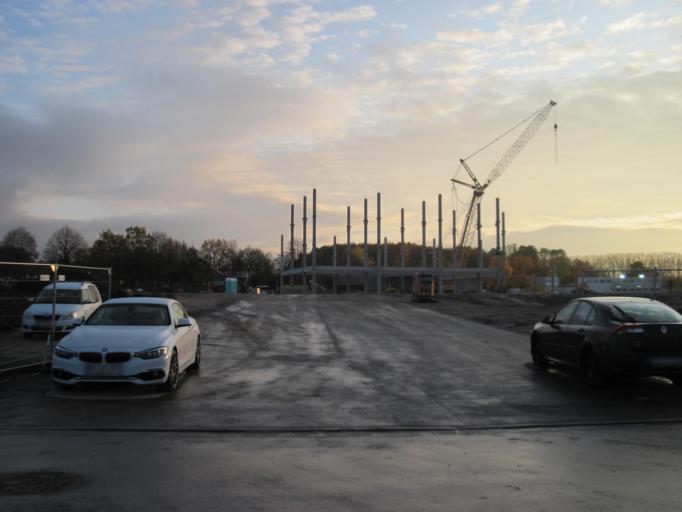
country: DE
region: North Rhine-Westphalia
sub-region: Regierungsbezirk Detmold
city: Paderborn
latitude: 51.7314
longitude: 8.7170
